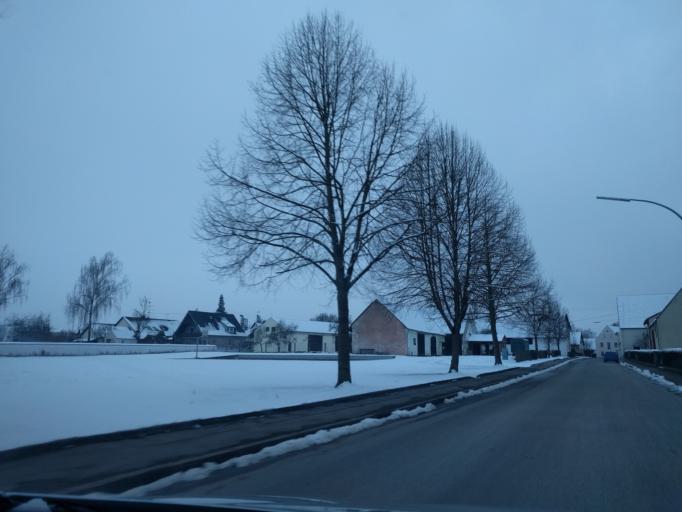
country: DE
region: Bavaria
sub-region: Swabia
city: Genderkingen
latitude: 48.7081
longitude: 10.8816
